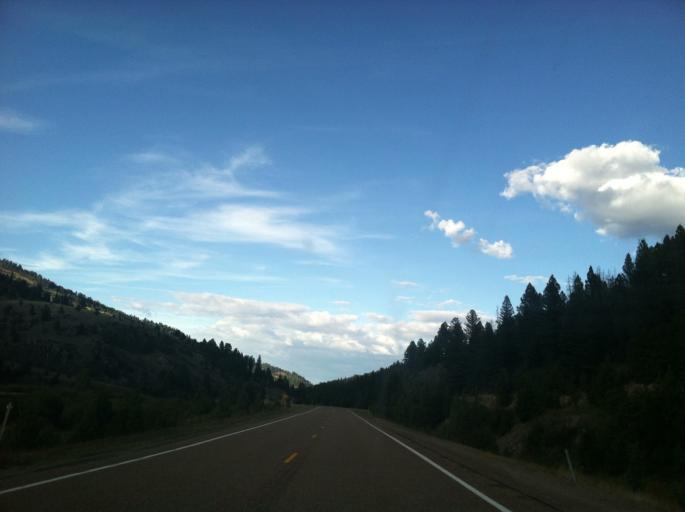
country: US
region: Montana
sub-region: Granite County
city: Philipsburg
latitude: 46.4202
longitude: -113.2813
